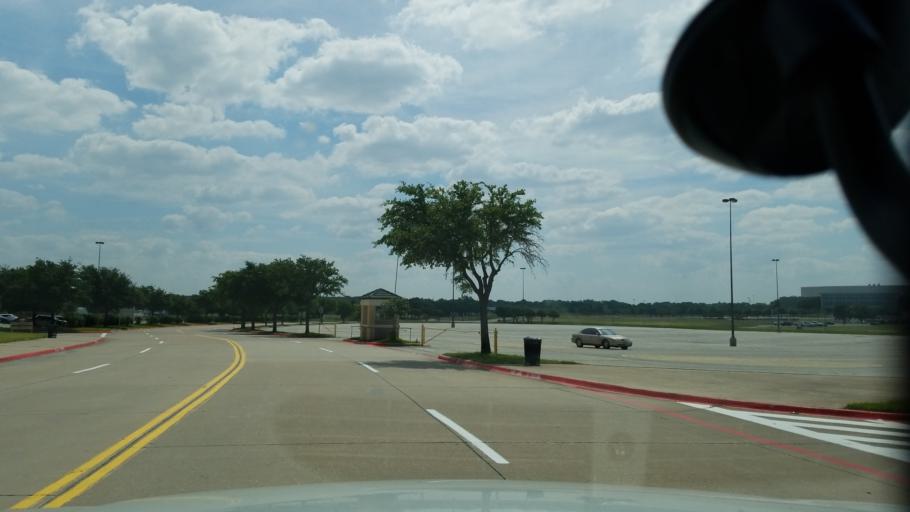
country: US
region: Texas
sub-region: Dallas County
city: Grand Prairie
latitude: 32.7713
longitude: -96.9882
